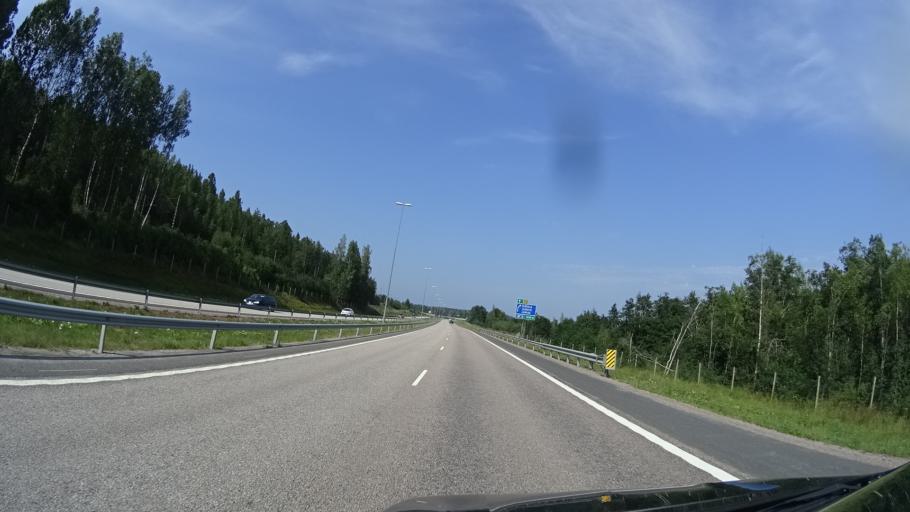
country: FI
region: Uusimaa
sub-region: Helsinki
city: Kirkkonummi
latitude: 60.1245
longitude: 24.4893
